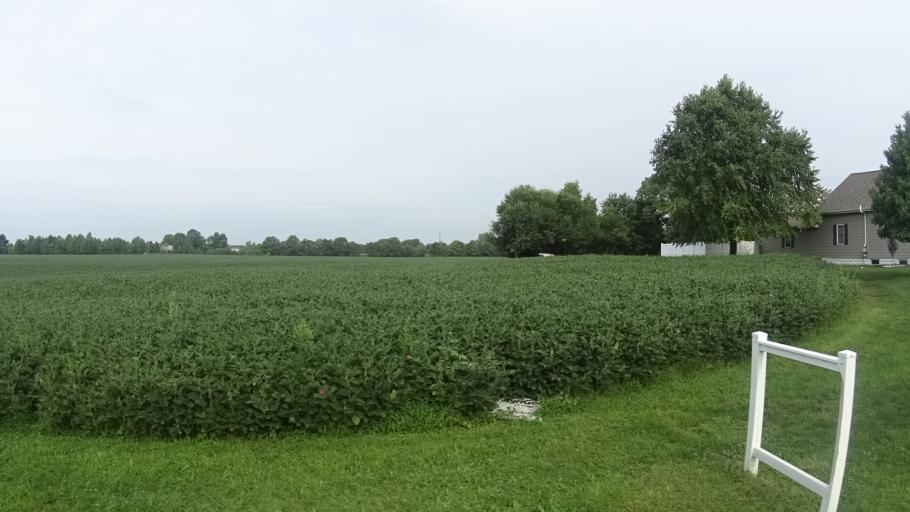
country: US
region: Indiana
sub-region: Madison County
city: Pendleton
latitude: 40.0203
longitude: -85.7387
